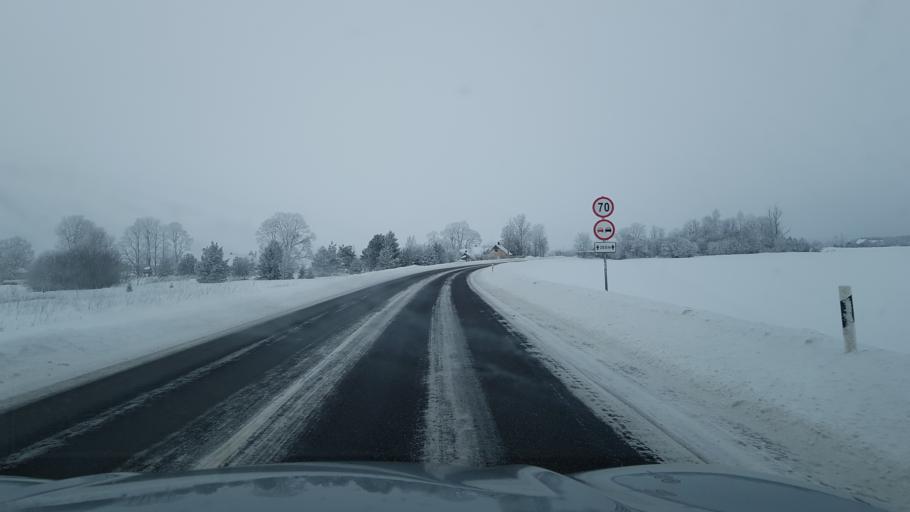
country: EE
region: Ida-Virumaa
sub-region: Johvi vald
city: Johvi
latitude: 59.3159
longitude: 27.3925
